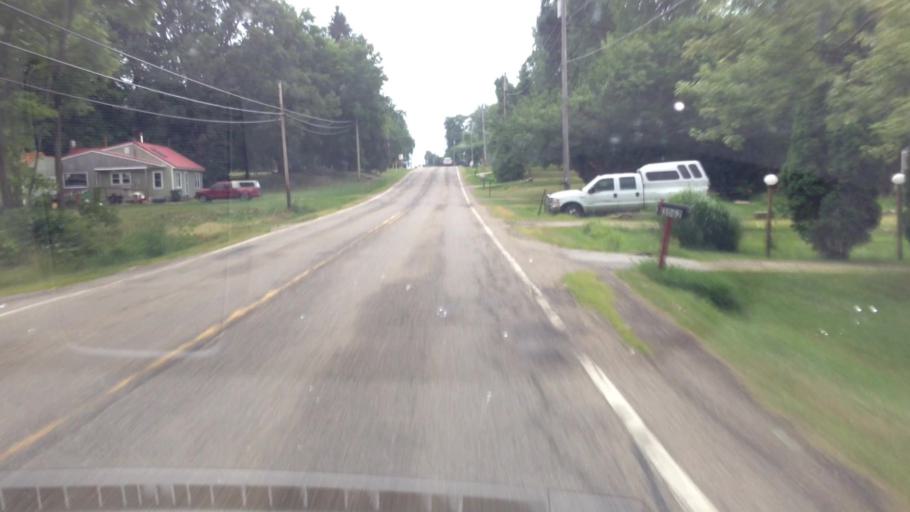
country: US
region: Ohio
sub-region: Summit County
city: Lakemore
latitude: 40.9837
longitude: -81.4462
